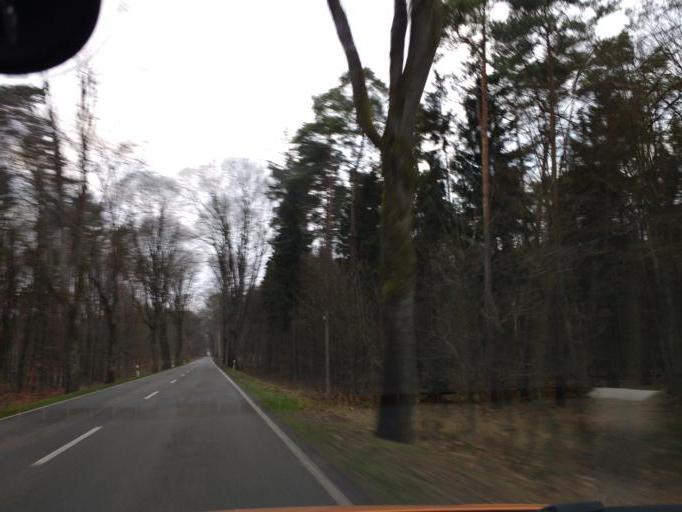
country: DE
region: Brandenburg
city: Strausberg
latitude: 52.6537
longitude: 13.8952
